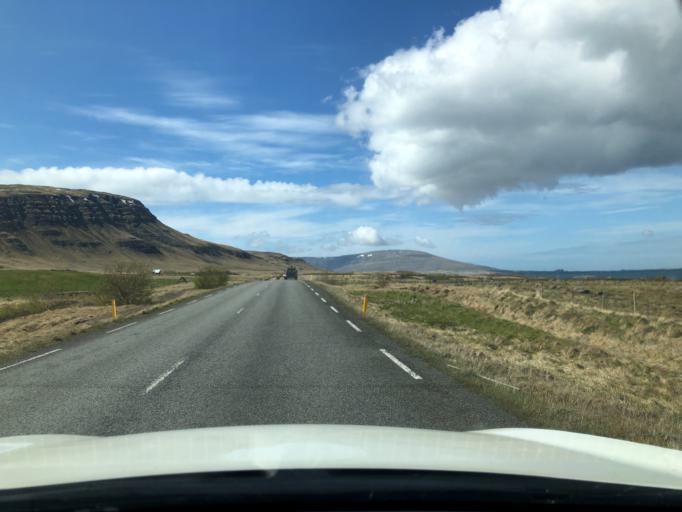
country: IS
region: Capital Region
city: Mosfellsbaer
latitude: 64.3302
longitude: -21.6461
